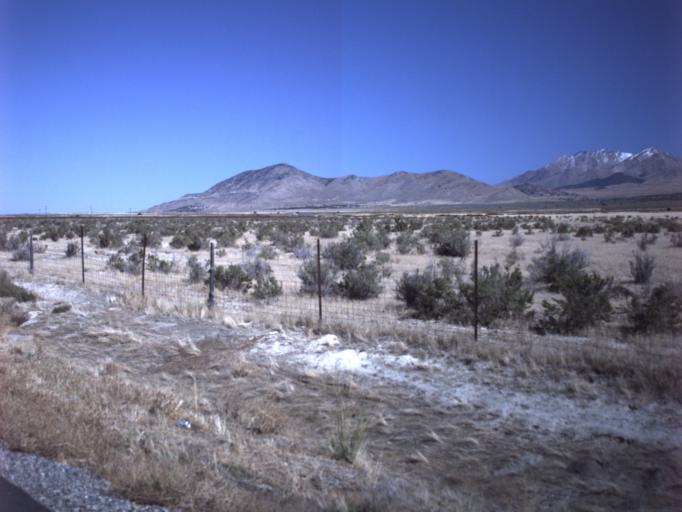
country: US
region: Utah
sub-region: Tooele County
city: Grantsville
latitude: 40.4867
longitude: -112.7462
